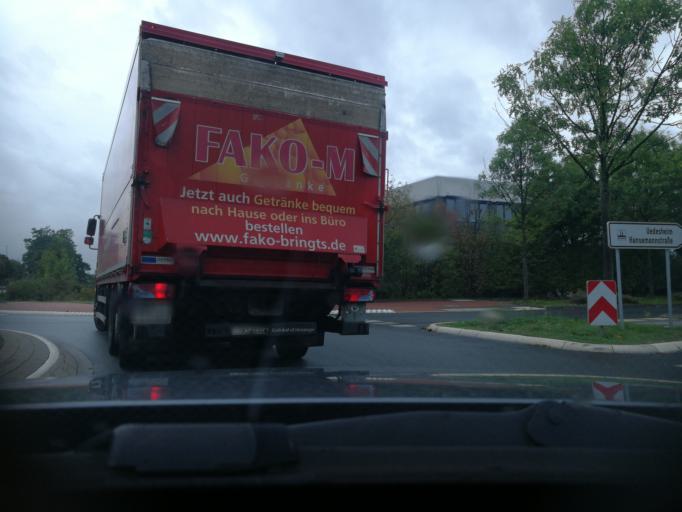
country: DE
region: North Rhine-Westphalia
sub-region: Regierungsbezirk Dusseldorf
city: Dusseldorf
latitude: 51.1577
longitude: 6.7719
